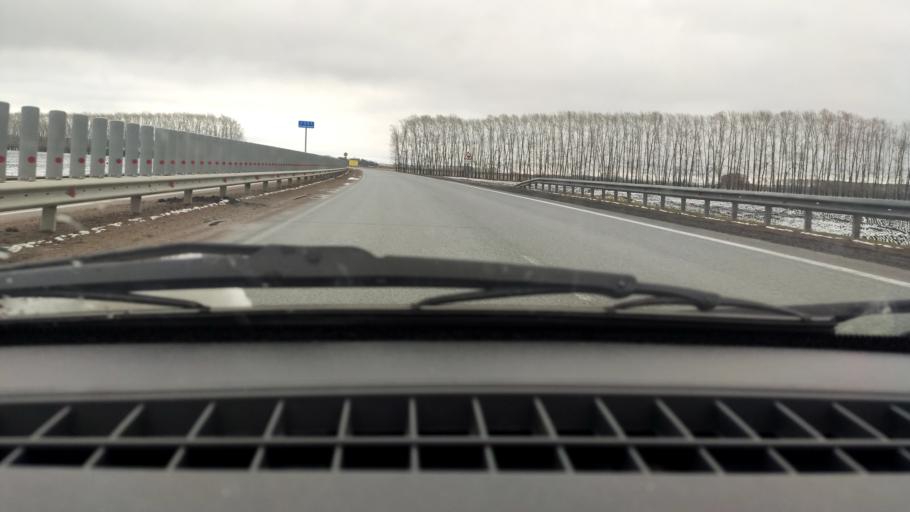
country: RU
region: Bashkortostan
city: Asanovo
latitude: 54.9828
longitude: 55.5302
